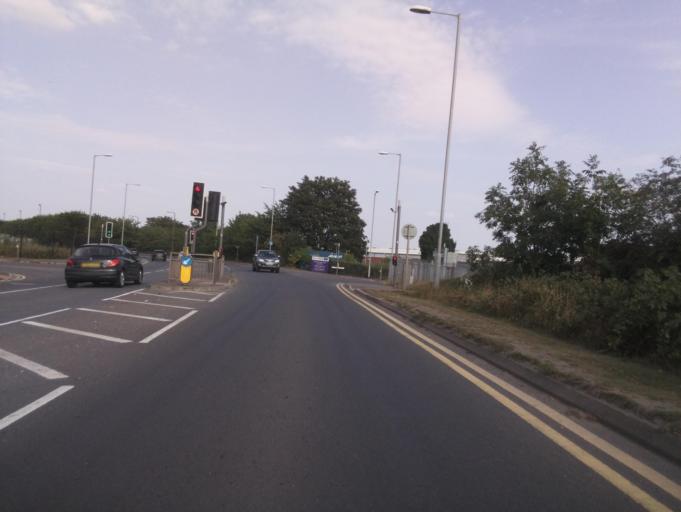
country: GB
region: England
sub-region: Staffordshire
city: Burton upon Trent
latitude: 52.7952
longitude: -1.6610
